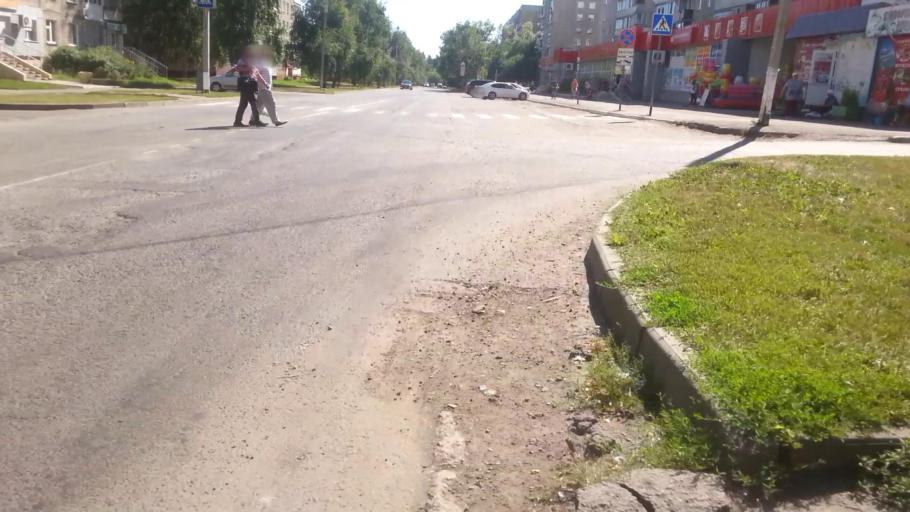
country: RU
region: Altai Krai
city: Novosilikatnyy
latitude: 53.3660
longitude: 83.6681
